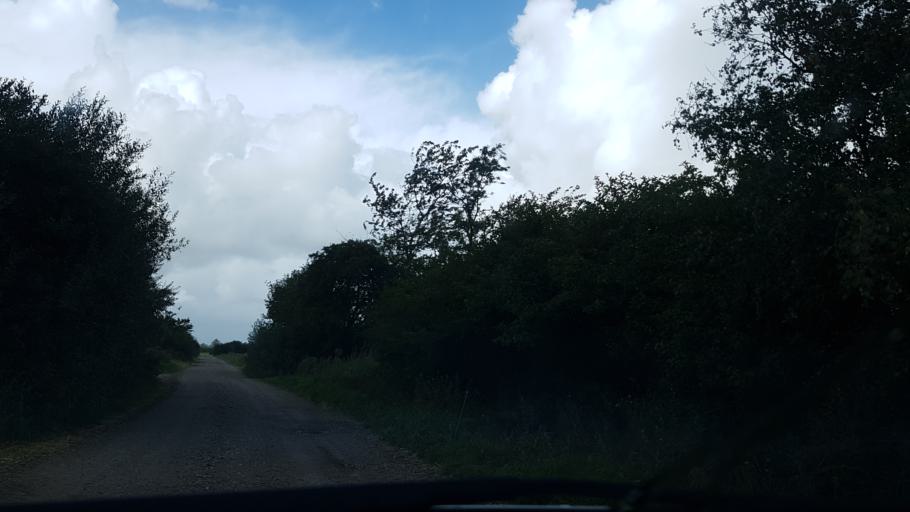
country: DK
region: South Denmark
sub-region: Tonder Kommune
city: Sherrebek
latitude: 55.2430
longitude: 8.7879
